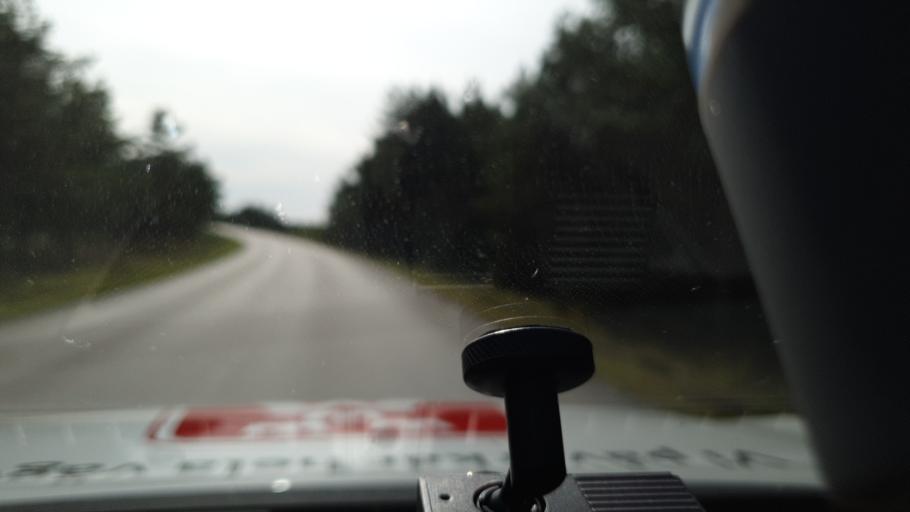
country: SE
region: Gotland
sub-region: Gotland
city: Slite
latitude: 57.8754
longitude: 19.0853
